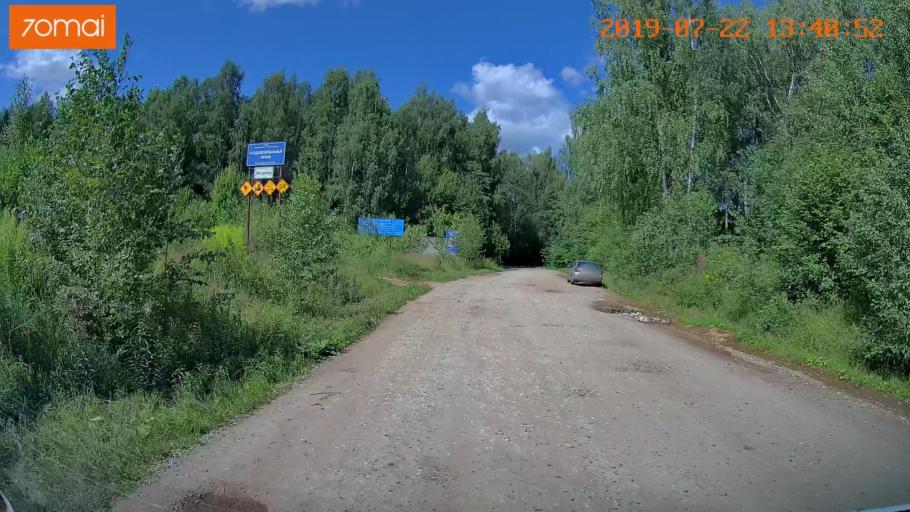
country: RU
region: Ivanovo
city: Novo-Talitsy
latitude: 57.0779
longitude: 40.8805
